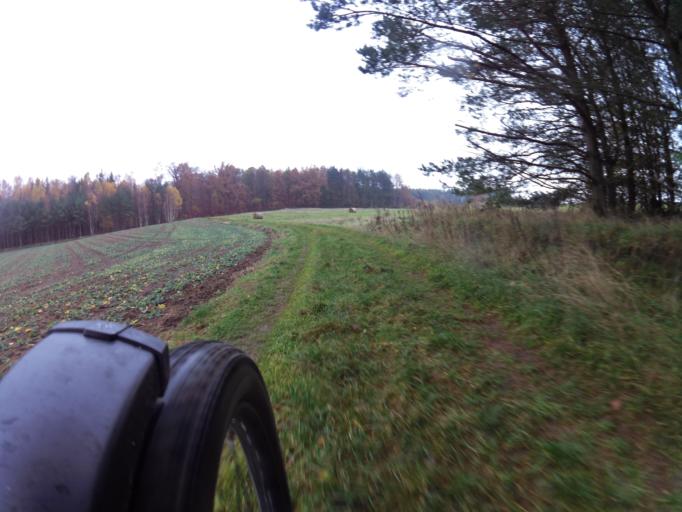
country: PL
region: Pomeranian Voivodeship
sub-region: Powiat pucki
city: Krokowa
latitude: 54.7292
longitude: 18.1318
